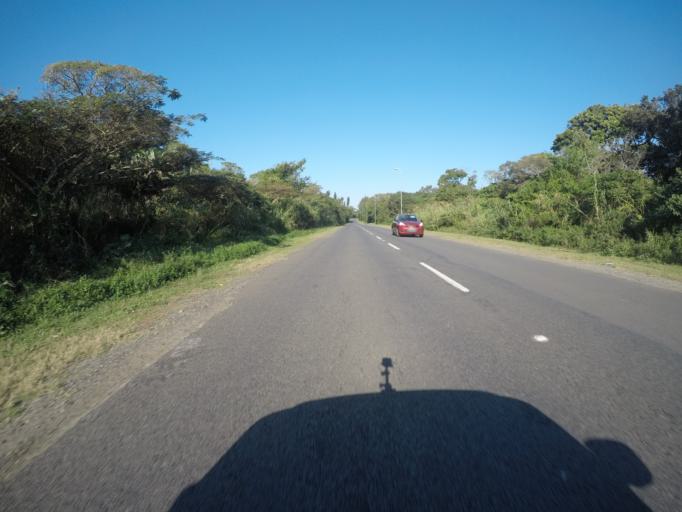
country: ZA
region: KwaZulu-Natal
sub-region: uThungulu District Municipality
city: Richards Bay
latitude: -28.7905
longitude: 32.0898
